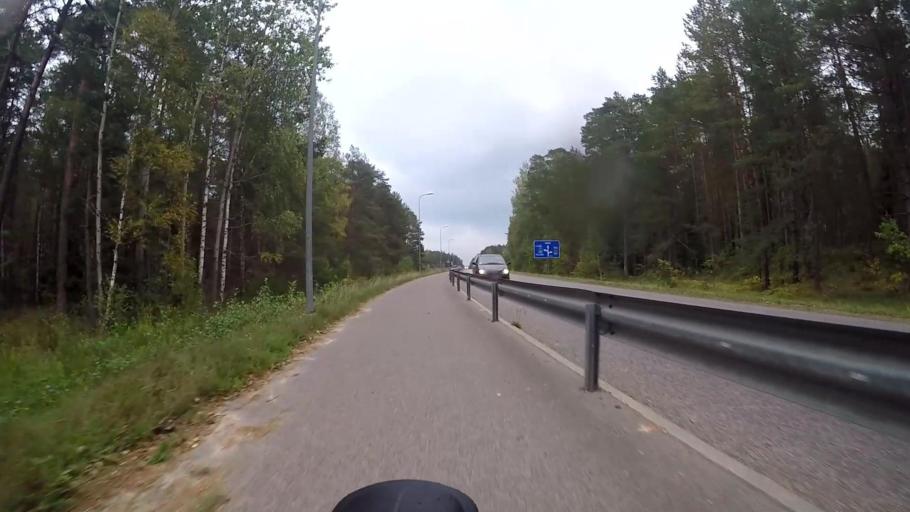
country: LV
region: Saulkrastu
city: Saulkrasti
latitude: 57.2680
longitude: 24.4323
